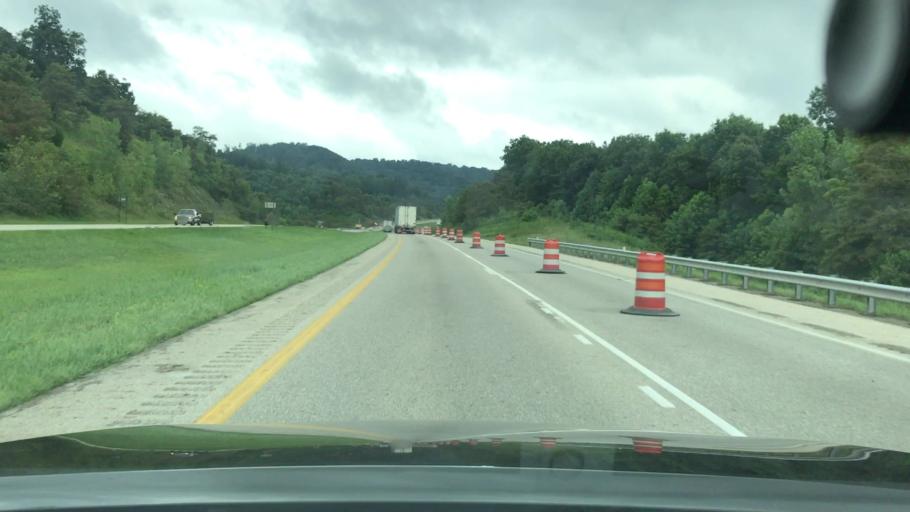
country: US
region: Ohio
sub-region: Ross County
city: Chillicothe
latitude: 39.2444
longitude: -82.8448
